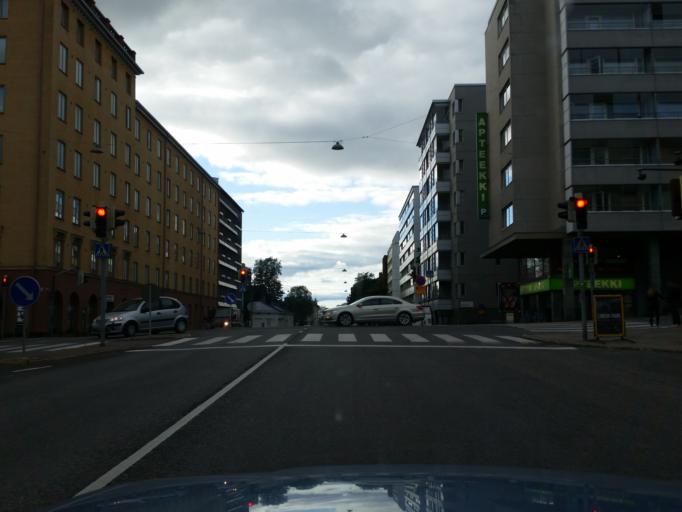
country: FI
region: Varsinais-Suomi
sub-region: Turku
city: Turku
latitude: 60.4448
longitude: 22.2752
